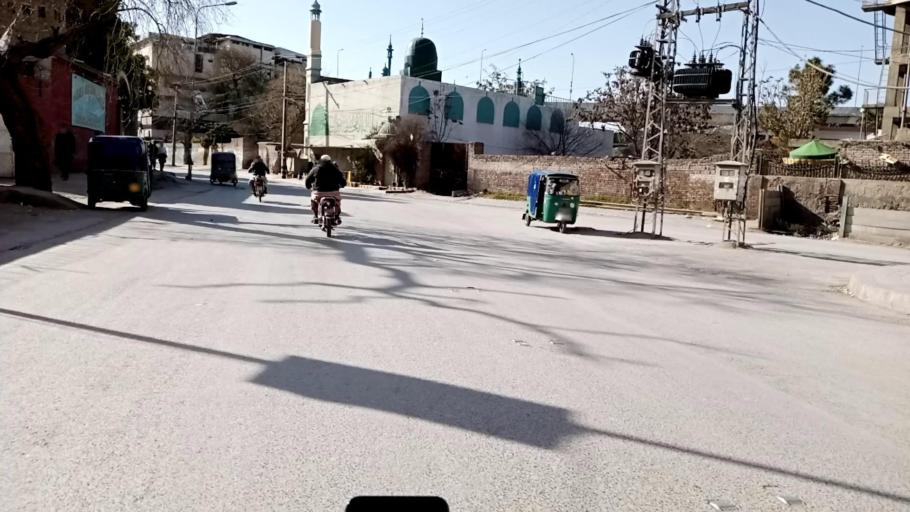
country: PK
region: Khyber Pakhtunkhwa
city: Peshawar
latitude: 34.0039
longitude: 71.5572
